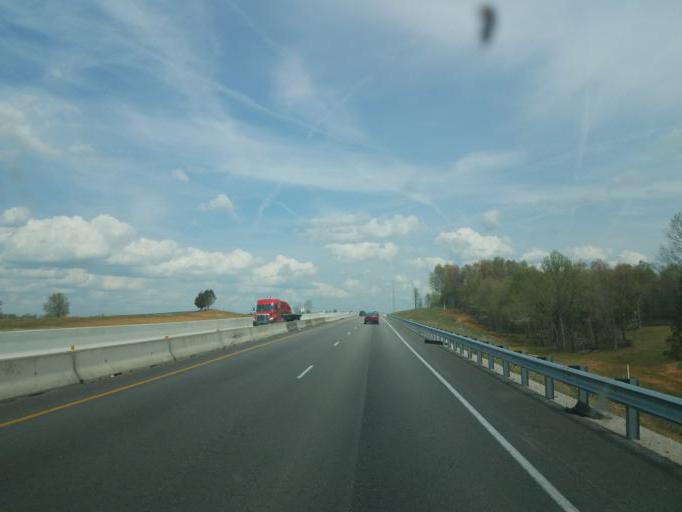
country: US
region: Kentucky
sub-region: Larue County
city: Hodgenville
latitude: 37.4777
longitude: -85.8813
